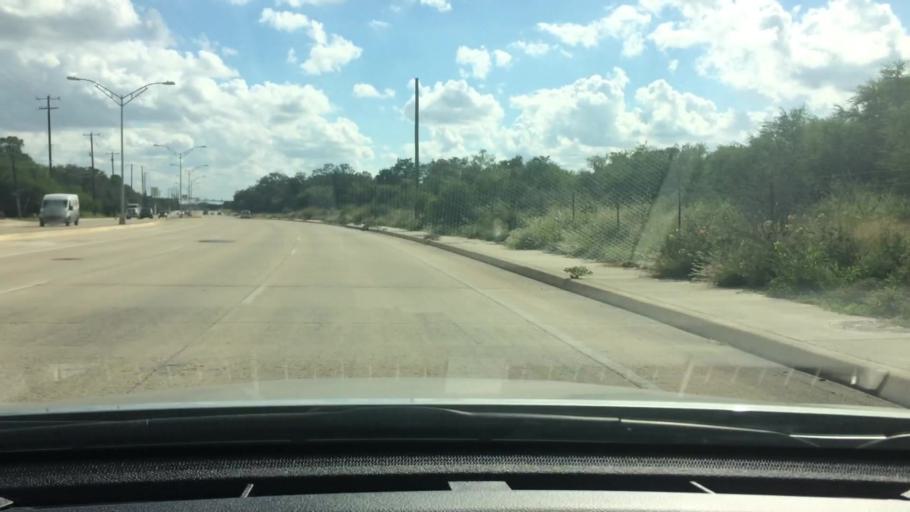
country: US
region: Texas
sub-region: Bexar County
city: Hollywood Park
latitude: 29.6262
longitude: -98.4239
